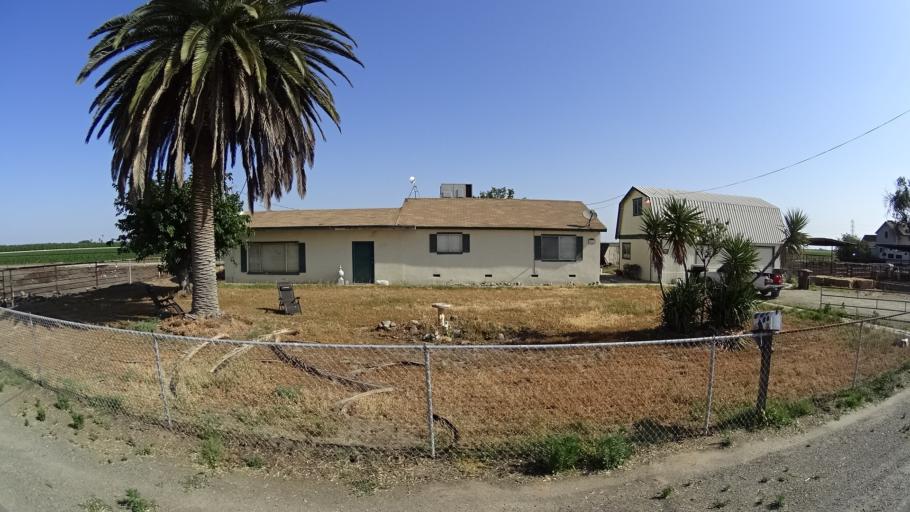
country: US
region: California
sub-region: Kings County
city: Home Garden
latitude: 36.2404
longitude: -119.5948
